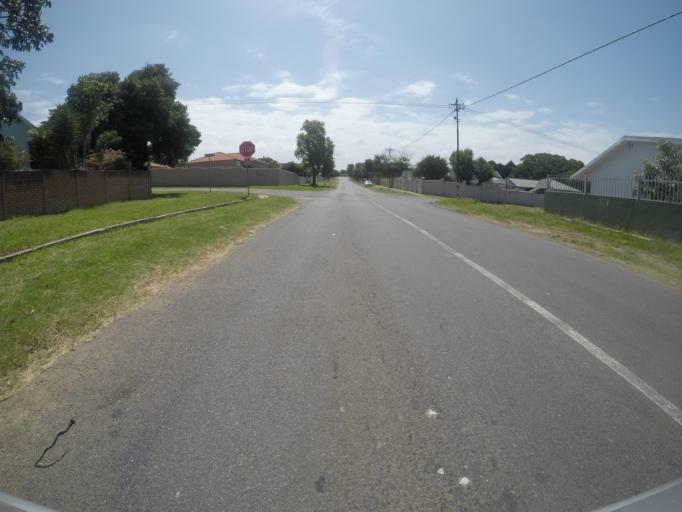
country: ZA
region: Eastern Cape
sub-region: Buffalo City Metropolitan Municipality
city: East London
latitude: -32.9767
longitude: 27.8733
